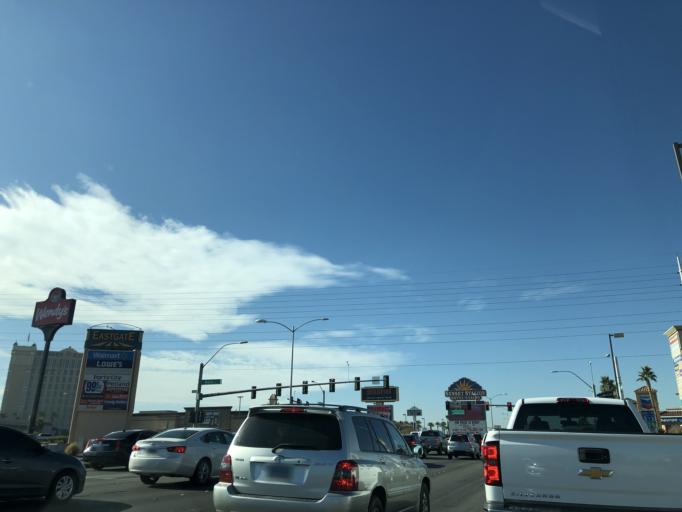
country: US
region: Nevada
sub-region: Clark County
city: Whitney
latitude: 36.0639
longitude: -115.0354
